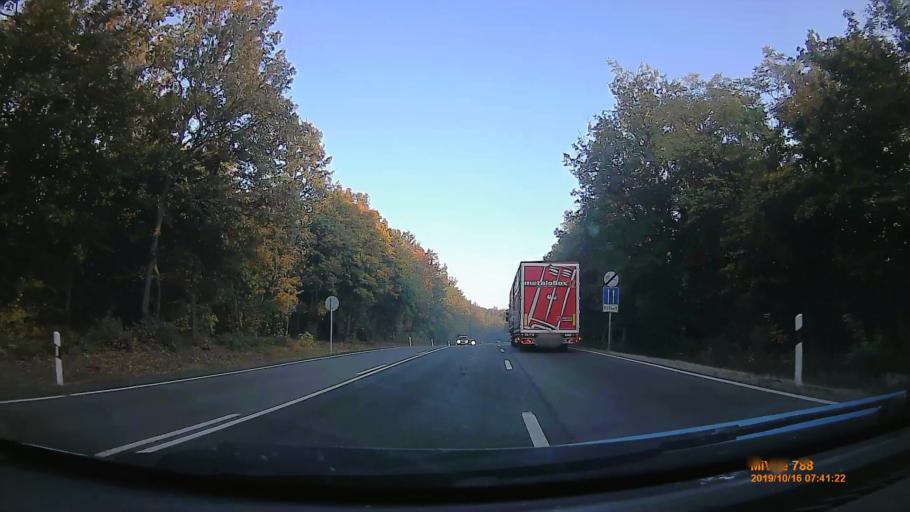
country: HU
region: Heves
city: Kerecsend
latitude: 47.8271
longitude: 20.3562
